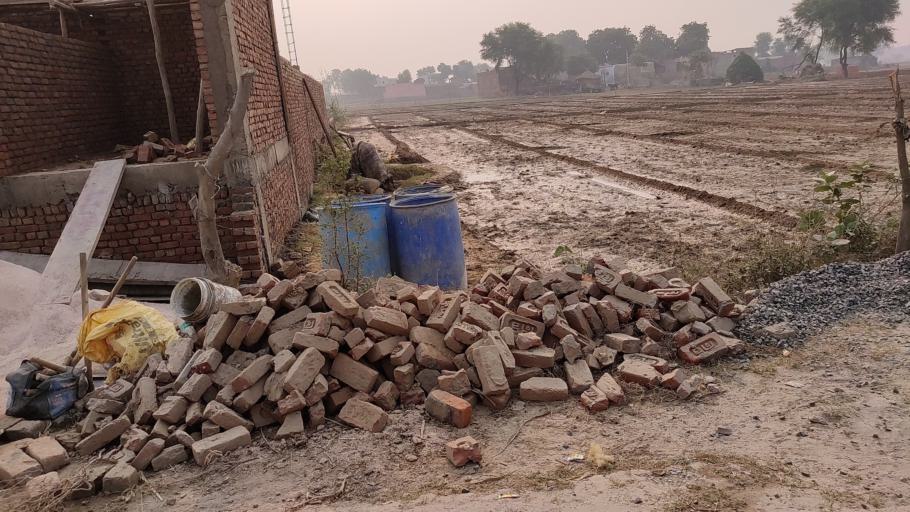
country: IN
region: Uttar Pradesh
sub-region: Mathura
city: Vrindavan
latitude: 27.5555
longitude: 77.7162
